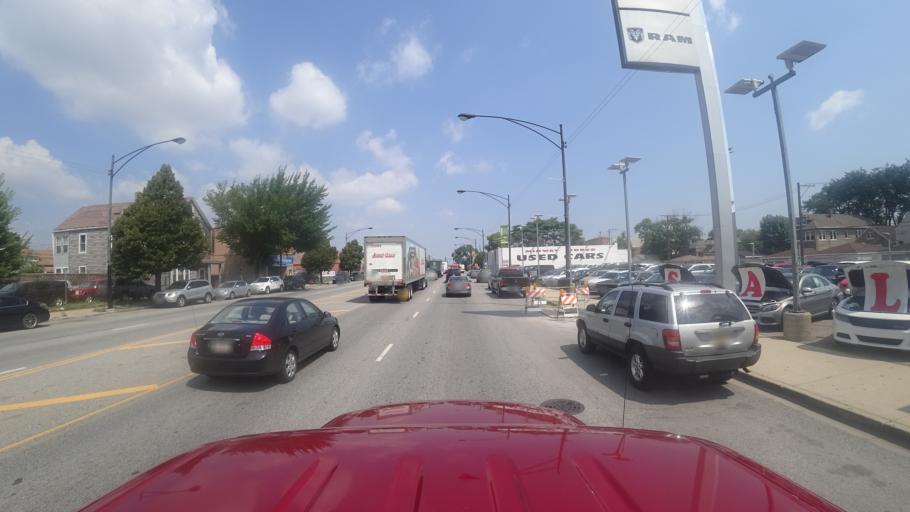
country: US
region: Illinois
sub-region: Cook County
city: Cicero
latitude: 41.8064
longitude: -87.7235
